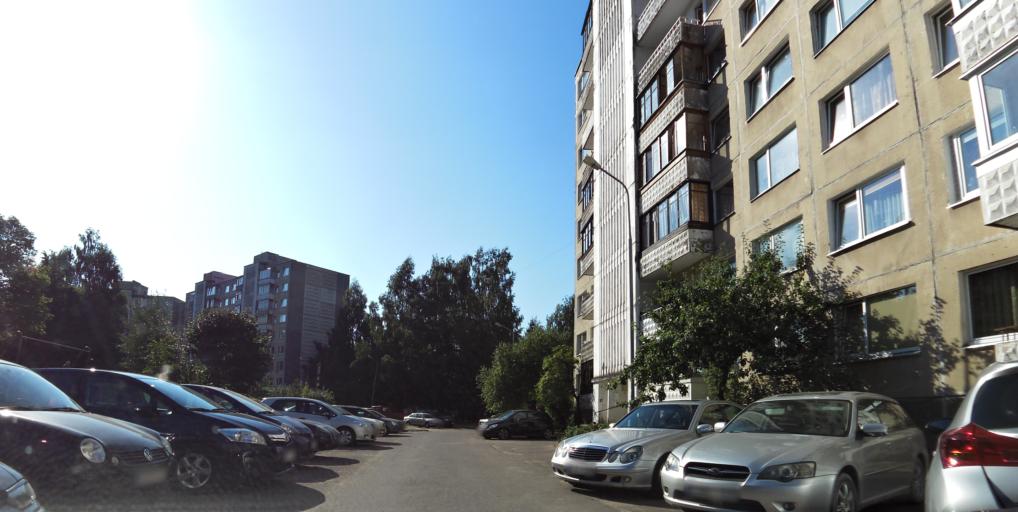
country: LT
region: Vilnius County
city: Justiniskes
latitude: 54.7063
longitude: 25.2224
